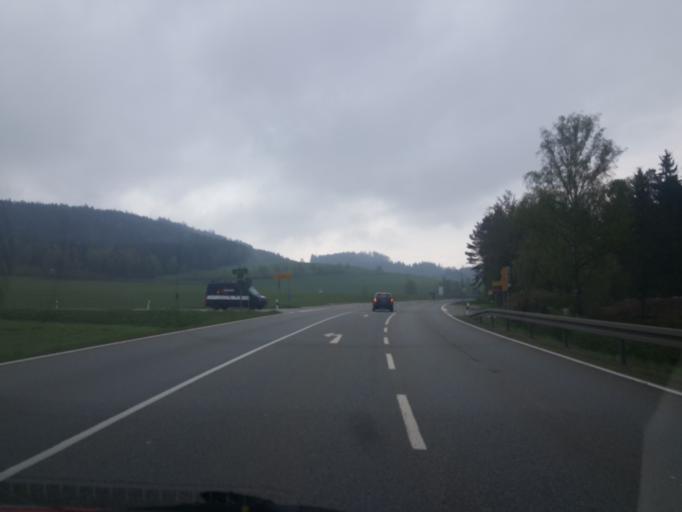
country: DE
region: Bavaria
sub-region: Lower Bavaria
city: Geiersthal
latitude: 49.0444
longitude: 12.9356
